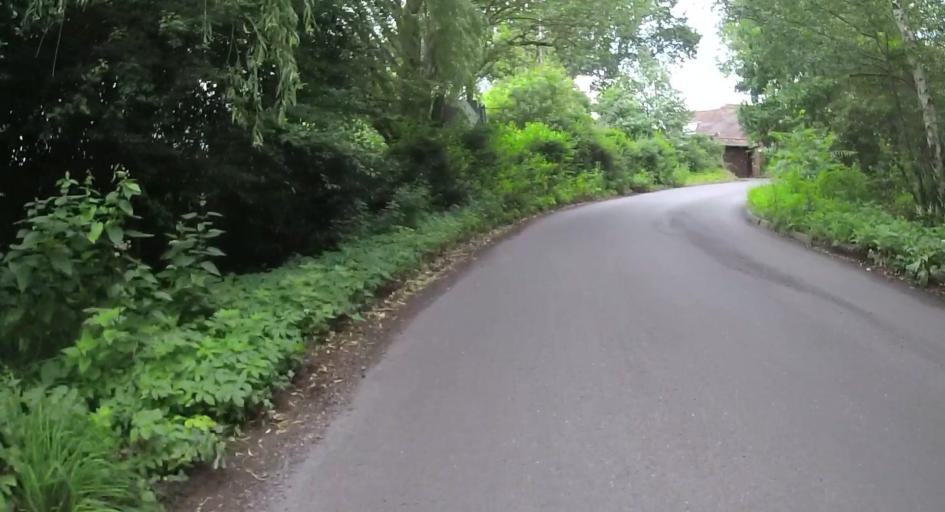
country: GB
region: England
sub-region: Bracknell Forest
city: Crowthorne
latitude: 51.3917
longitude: -0.8120
